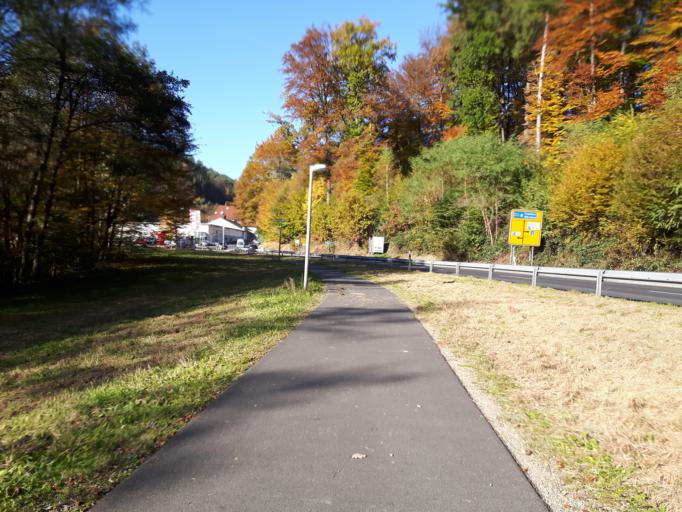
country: DE
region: Bavaria
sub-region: Regierungsbezirk Unterfranken
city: Mespelbrunn
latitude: 49.9030
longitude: 9.2995
